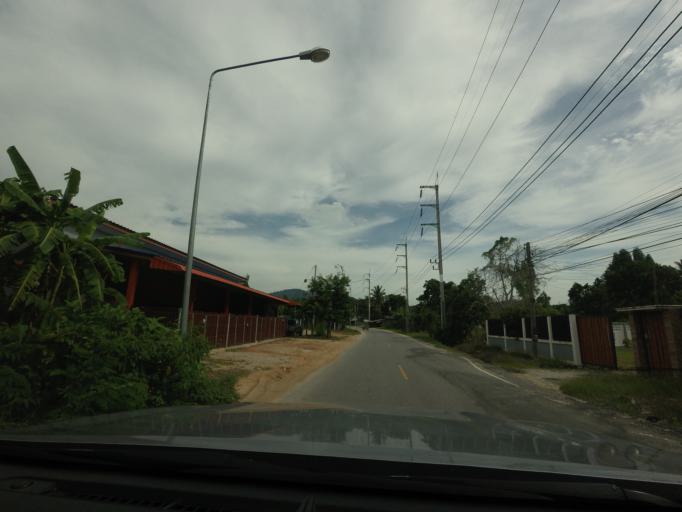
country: TH
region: Yala
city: Yala
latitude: 6.5204
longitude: 101.2888
